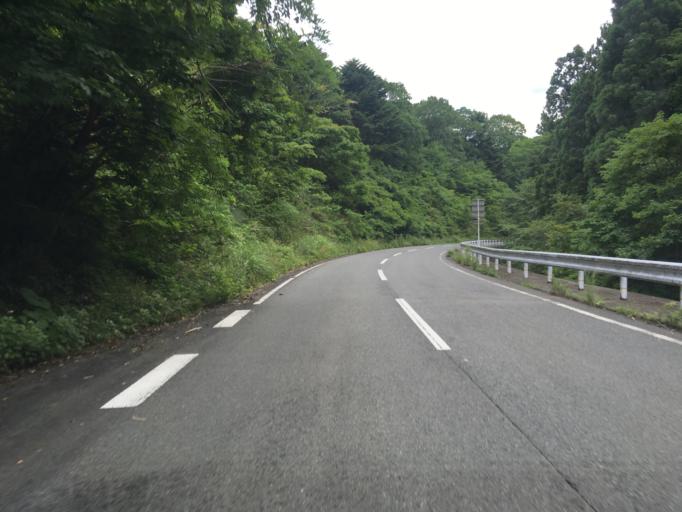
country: JP
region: Miyagi
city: Marumori
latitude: 37.7005
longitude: 140.8796
